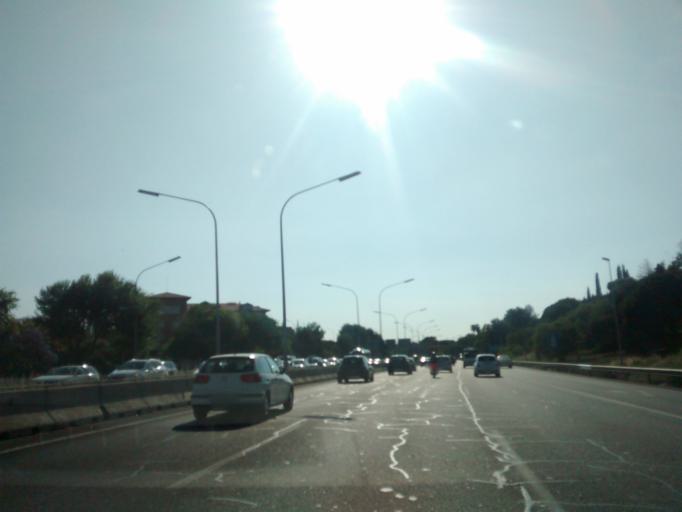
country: ES
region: Catalonia
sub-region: Provincia de Barcelona
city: Esplugues de Llobregat
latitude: 41.3809
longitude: 2.0942
